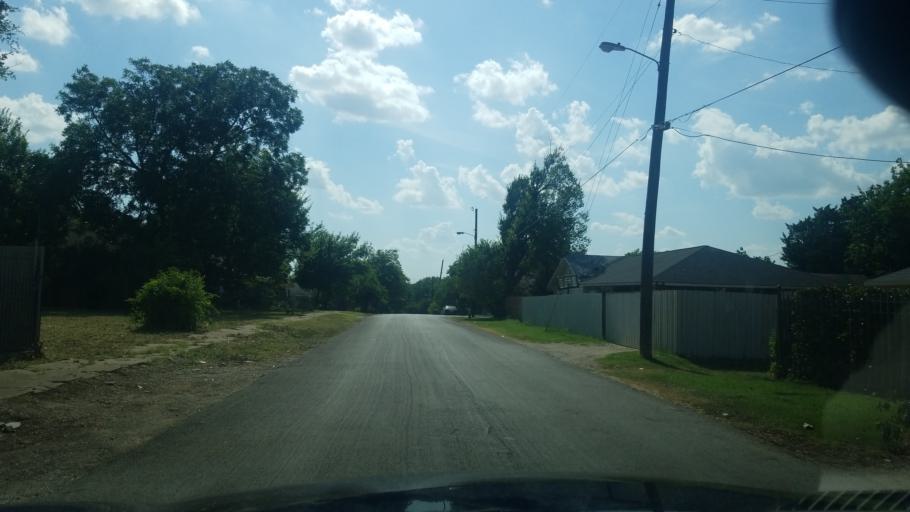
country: US
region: Texas
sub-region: Dallas County
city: Dallas
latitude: 32.7271
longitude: -96.8059
